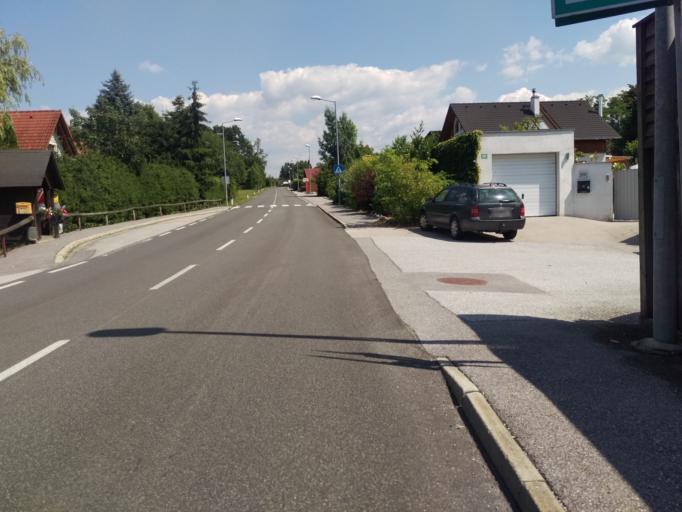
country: AT
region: Styria
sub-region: Politischer Bezirk Graz-Umgebung
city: Kumberg
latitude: 47.1447
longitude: 15.5147
